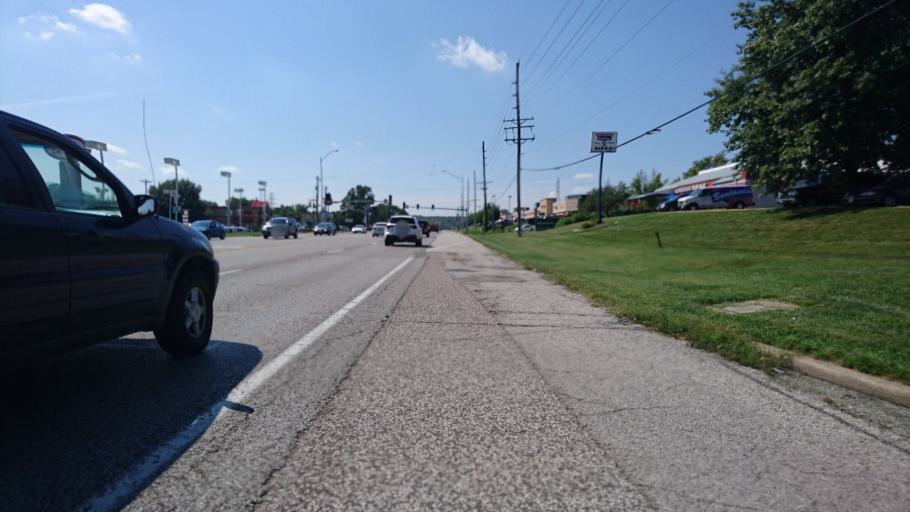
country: US
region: Missouri
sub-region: Saint Louis County
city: Manchester
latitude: 38.5945
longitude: -90.4950
